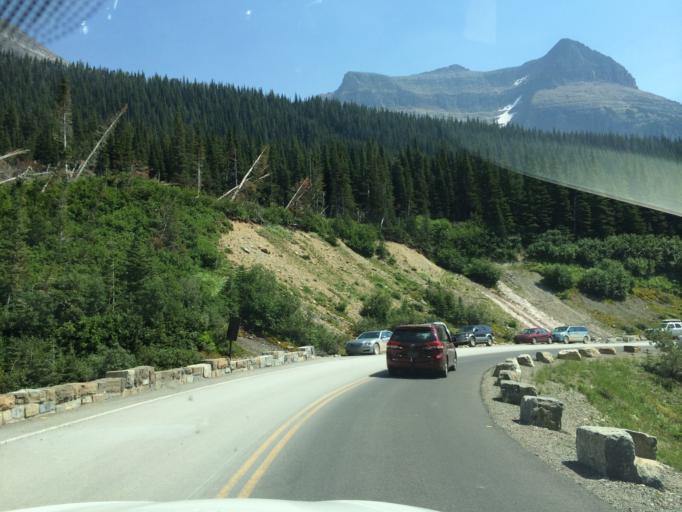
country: US
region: Montana
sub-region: Flathead County
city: Columbia Falls
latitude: 48.7016
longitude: -113.6678
